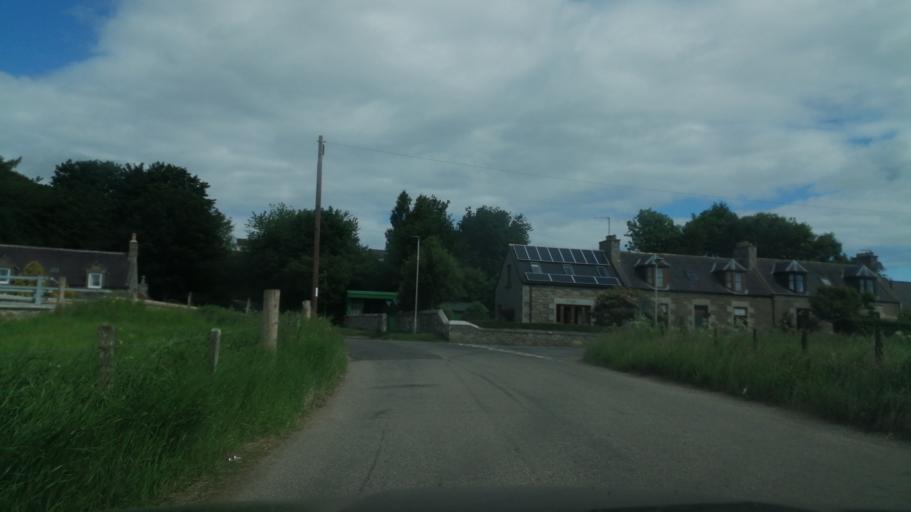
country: GB
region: Scotland
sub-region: Moray
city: Keith
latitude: 57.5554
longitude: -2.9474
